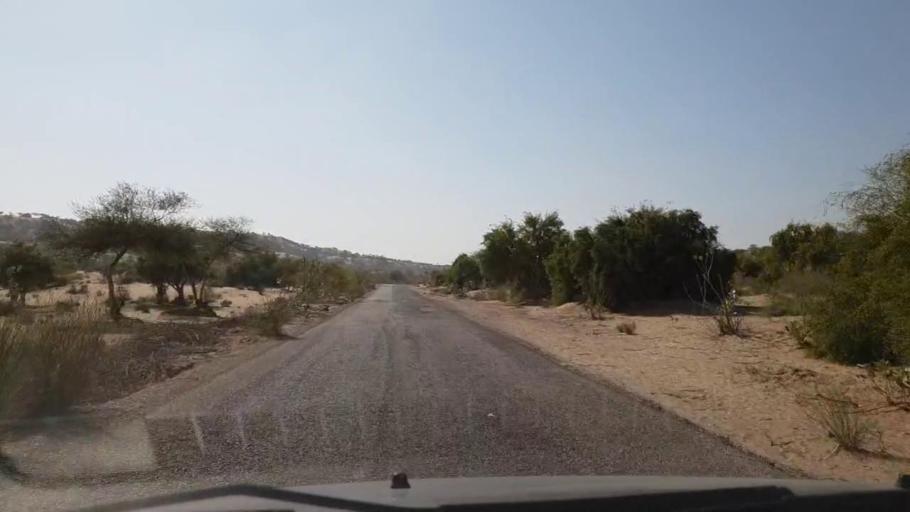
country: PK
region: Sindh
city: Diplo
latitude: 24.5837
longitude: 69.7037
